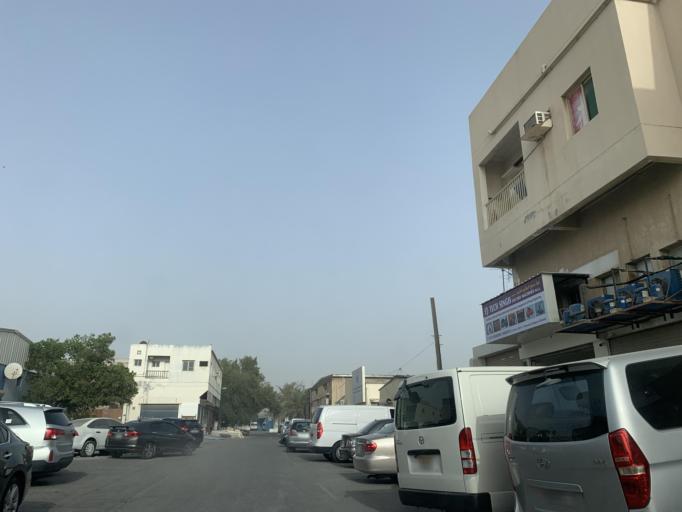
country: BH
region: Northern
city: Madinat `Isa
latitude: 26.1801
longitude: 50.5303
